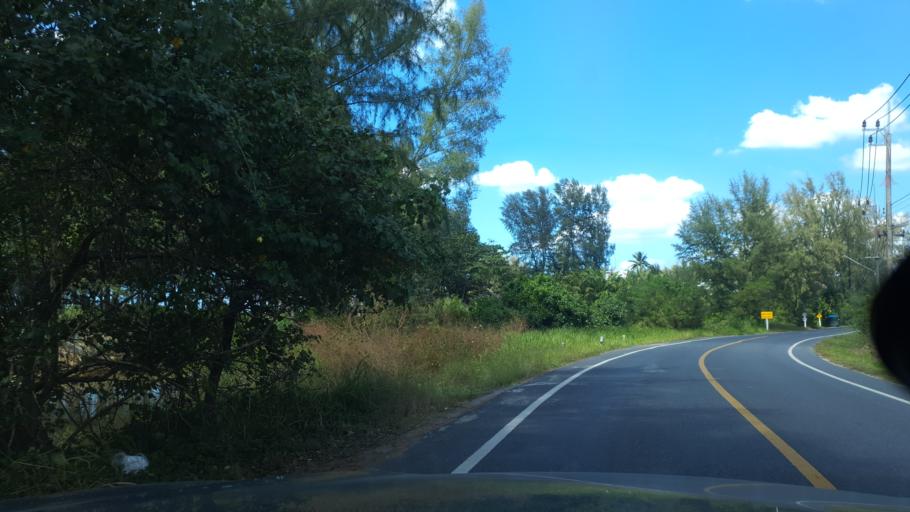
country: TH
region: Phangnga
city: Thai Mueang
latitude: 8.2847
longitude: 98.2752
